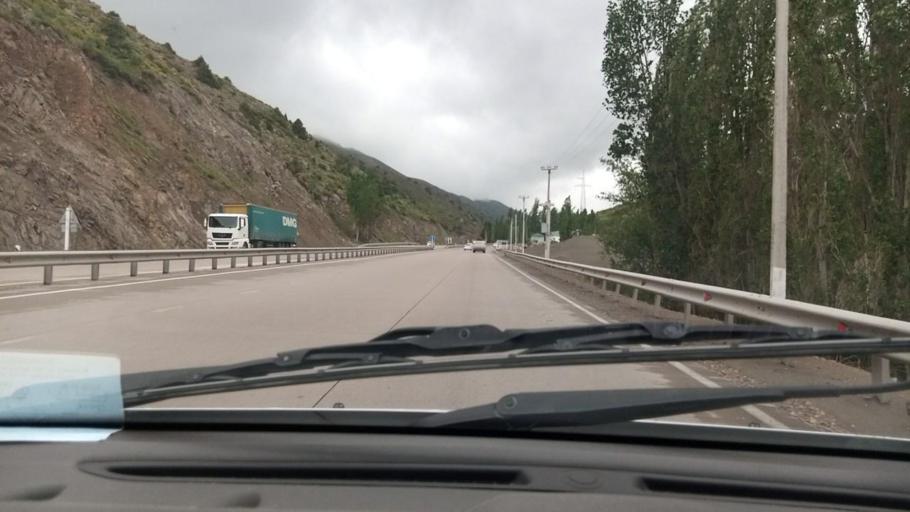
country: TJ
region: Viloyati Sughd
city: Shaydon
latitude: 41.0376
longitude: 70.5807
